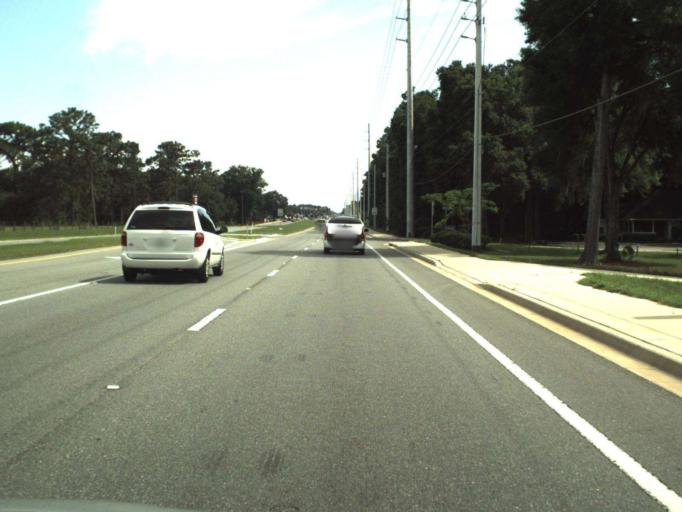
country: US
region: Florida
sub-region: Marion County
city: Silver Springs Shores
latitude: 29.1780
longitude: -82.0538
